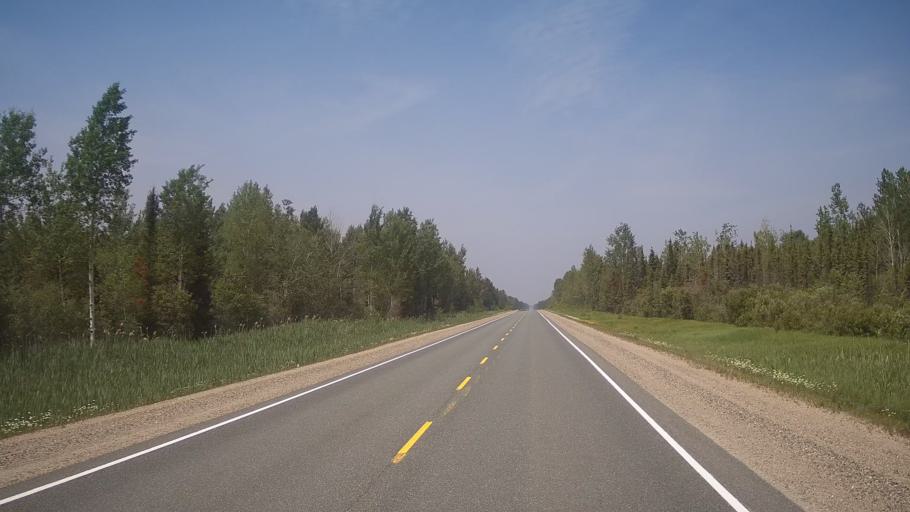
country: CA
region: Ontario
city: Timmins
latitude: 48.8233
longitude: -81.3709
